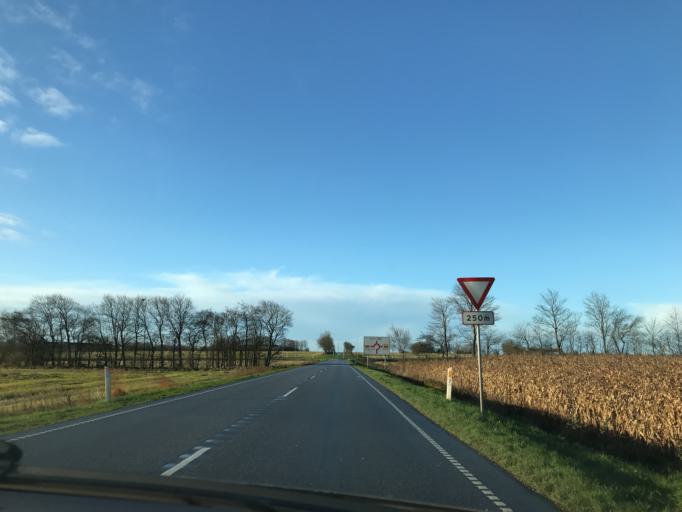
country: DK
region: South Denmark
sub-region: Haderslev Kommune
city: Vojens
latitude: 55.1632
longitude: 9.2805
